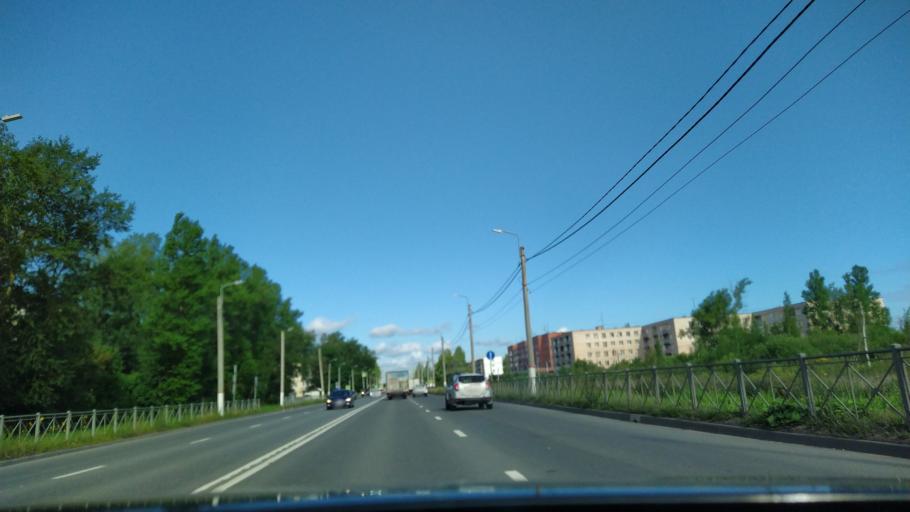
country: RU
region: Leningrad
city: Tosno
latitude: 59.5554
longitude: 30.8508
